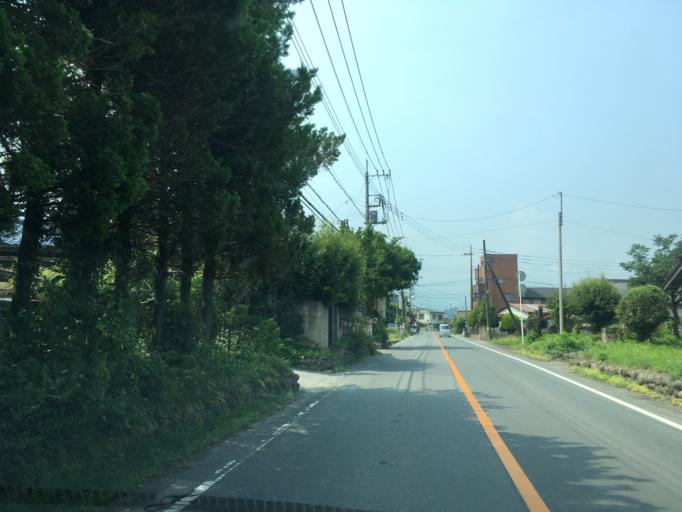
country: JP
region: Saitama
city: Chichibu
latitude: 36.0009
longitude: 139.1060
